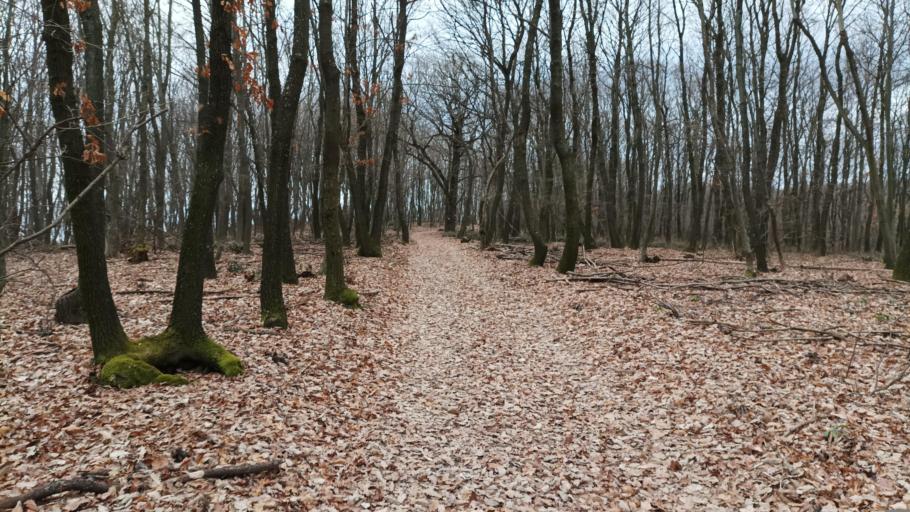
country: HU
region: Tolna
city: Szentgalpuszta
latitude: 46.3328
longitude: 18.6343
